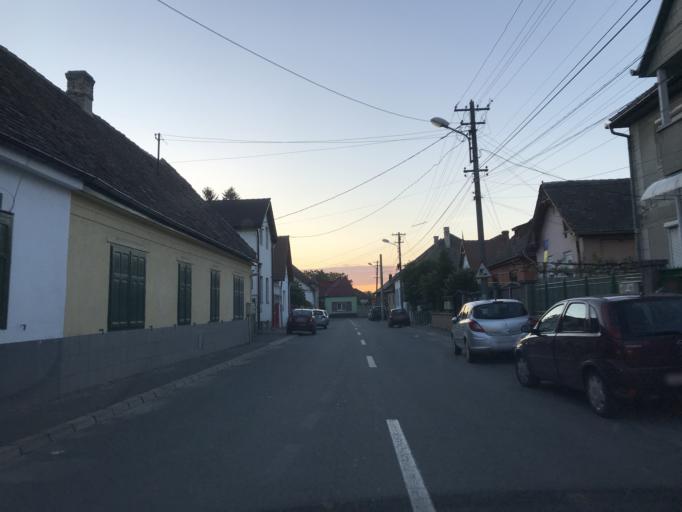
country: RO
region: Sibiu
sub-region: Municipiul Sibiu
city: Sibiu
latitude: 45.8028
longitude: 24.1651
